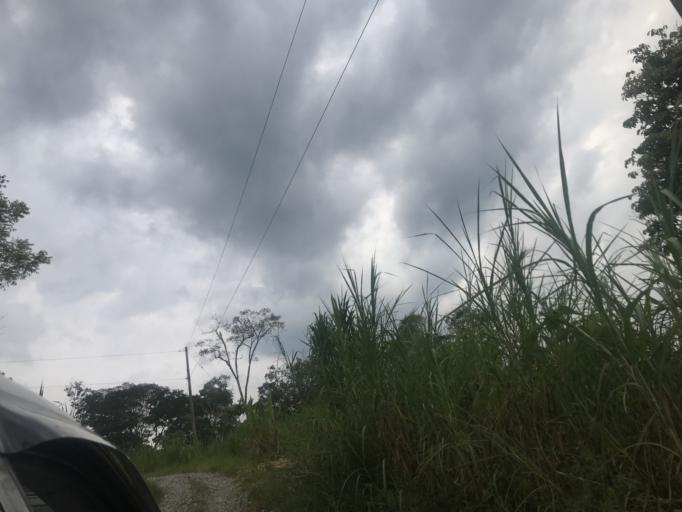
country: EC
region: Napo
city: Tena
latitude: -1.0223
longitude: -77.7417
